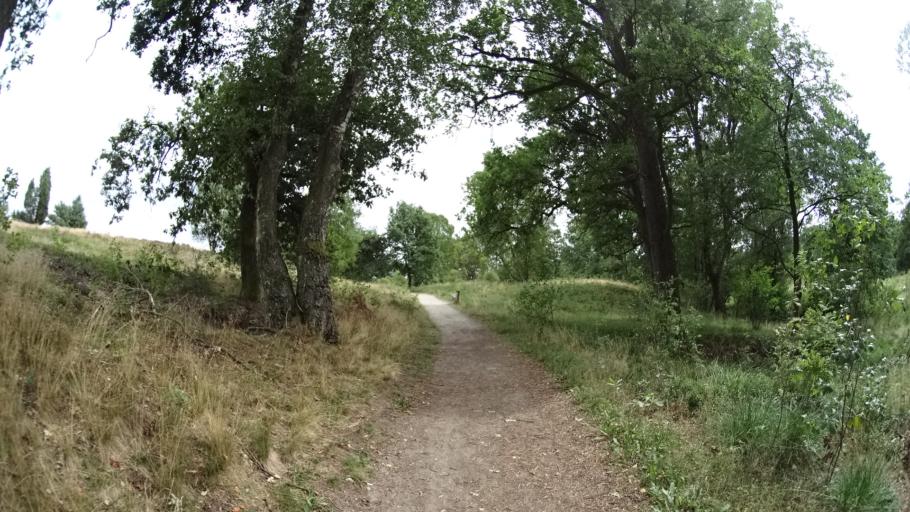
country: DE
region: Lower Saxony
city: Undeloh
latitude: 53.1900
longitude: 9.9811
